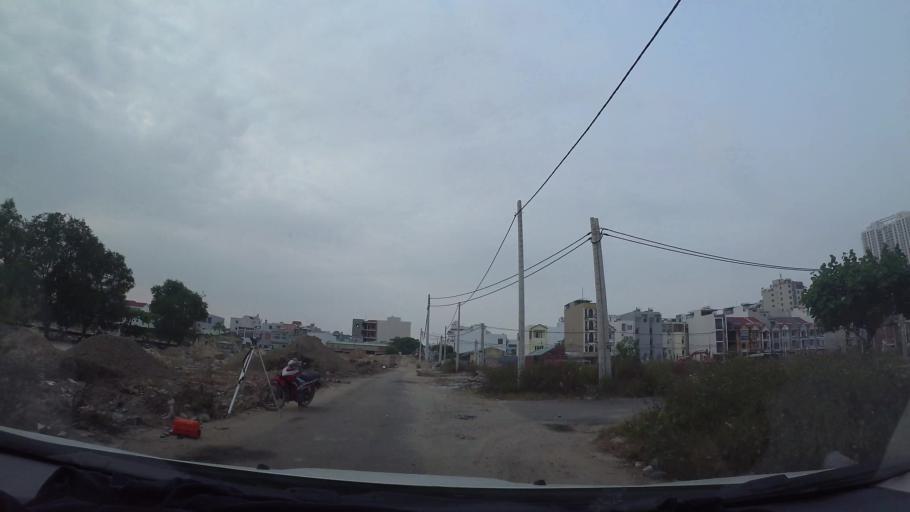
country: VN
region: Da Nang
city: Son Tra
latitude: 16.0500
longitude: 108.2430
